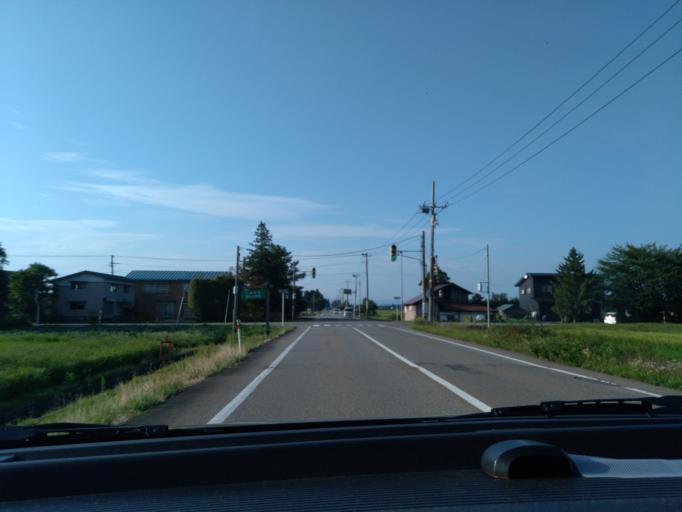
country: JP
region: Akita
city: Kakunodatemachi
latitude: 39.5196
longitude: 140.5584
